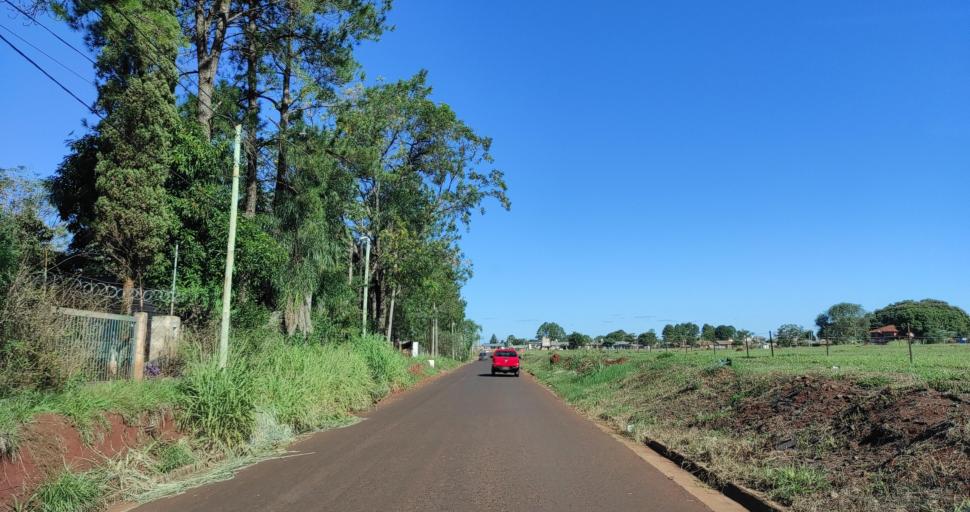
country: AR
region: Misiones
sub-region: Departamento de Capital
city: Posadas
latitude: -27.4266
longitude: -55.9295
